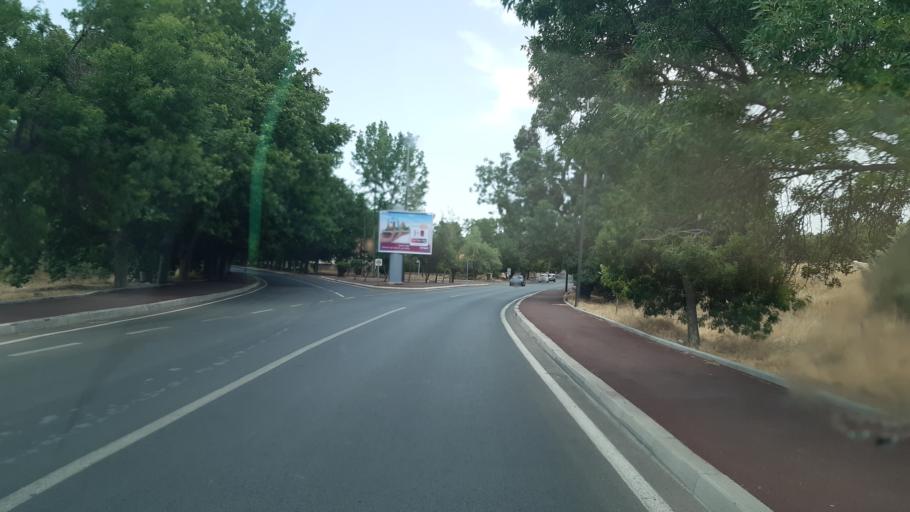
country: MA
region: Meknes-Tafilalet
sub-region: Ifrane
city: Ifrane
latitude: 33.5190
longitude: -5.1162
